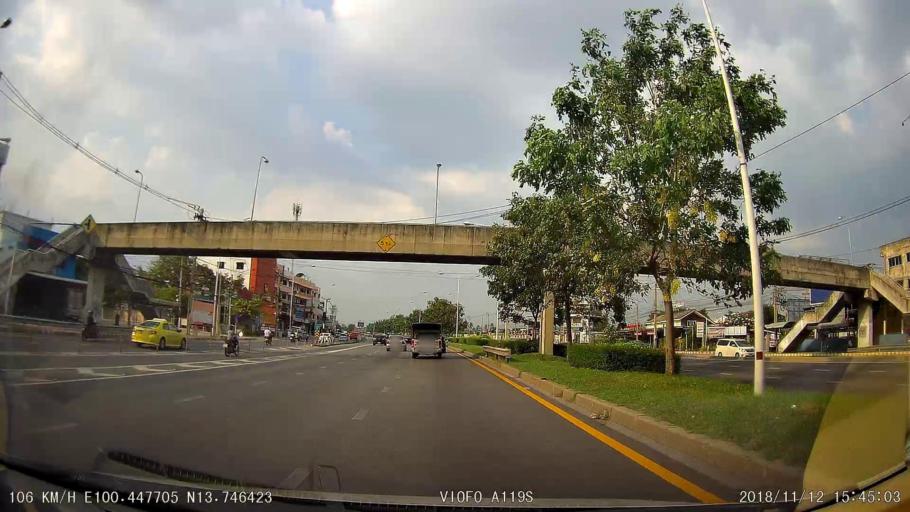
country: TH
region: Bangkok
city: Taling Chan
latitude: 13.7465
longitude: 100.4477
